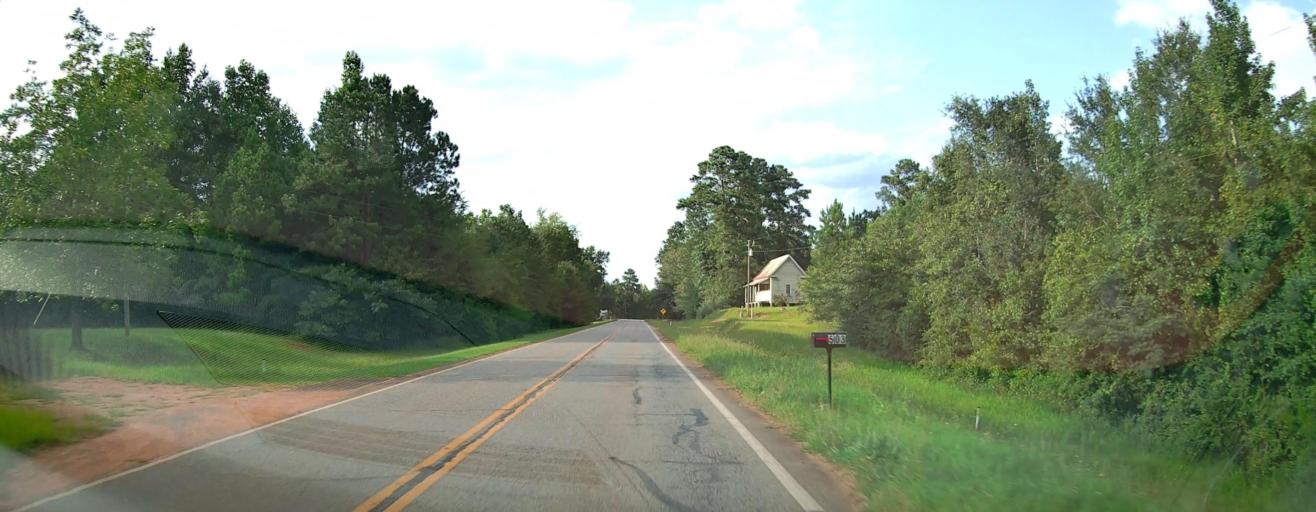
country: US
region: Georgia
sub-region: Crawford County
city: Roberta
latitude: 32.8048
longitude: -84.0301
